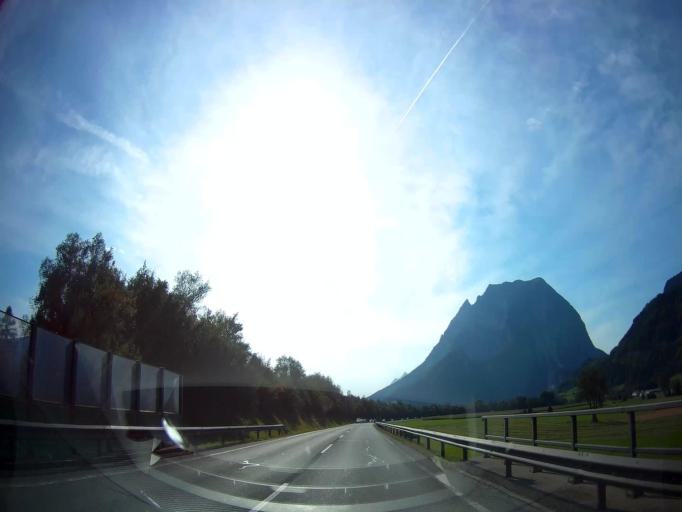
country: AT
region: Styria
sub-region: Politischer Bezirk Liezen
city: Stainach
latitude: 47.5267
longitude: 14.1096
